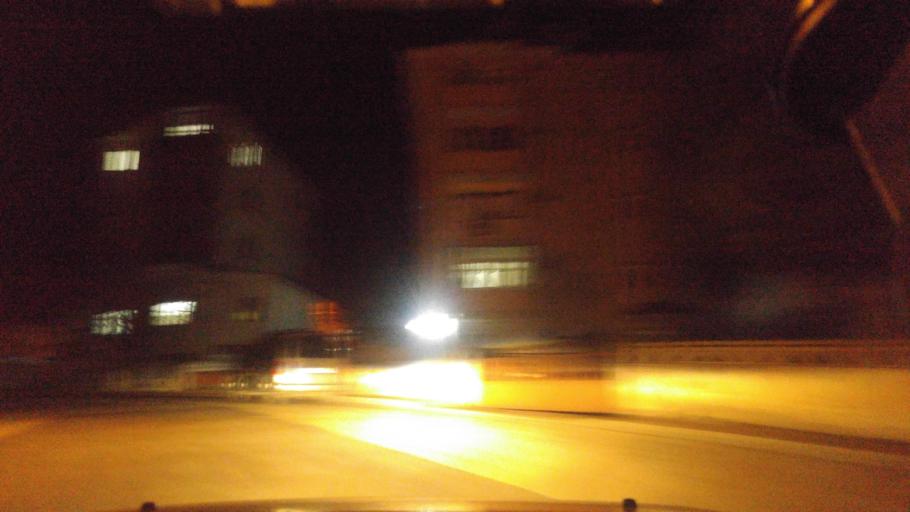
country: TR
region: Karabuk
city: Safranbolu
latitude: 41.2522
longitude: 32.6758
